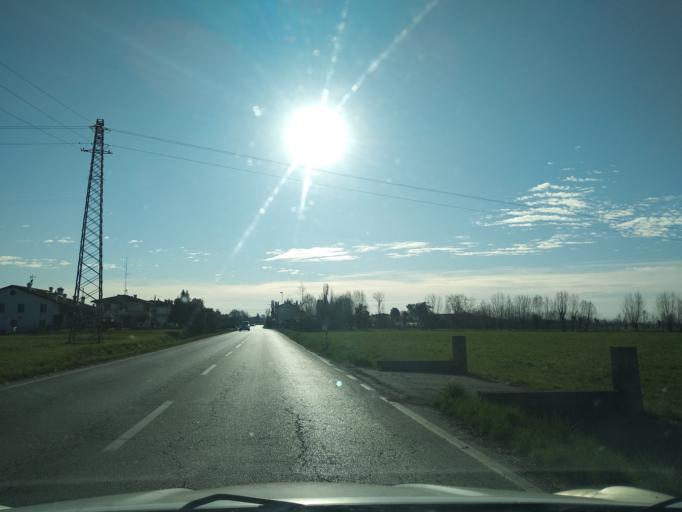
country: IT
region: Veneto
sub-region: Provincia di Vicenza
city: Quinto Vicentino
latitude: 45.5860
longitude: 11.6526
